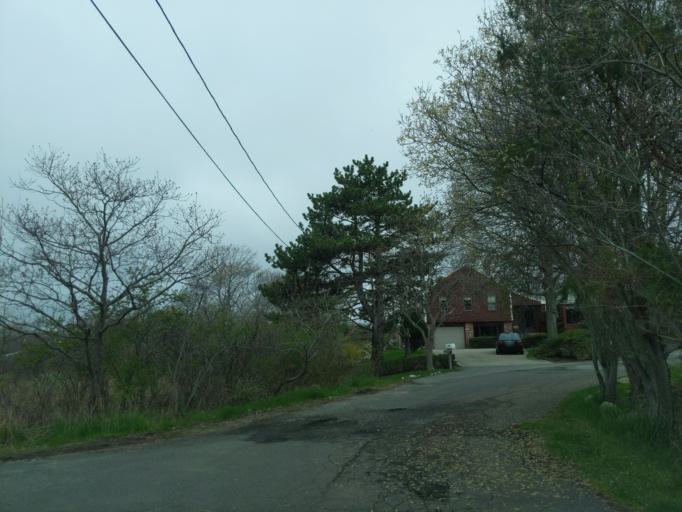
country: US
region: Massachusetts
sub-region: Essex County
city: Rockport
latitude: 42.6489
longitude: -70.6004
